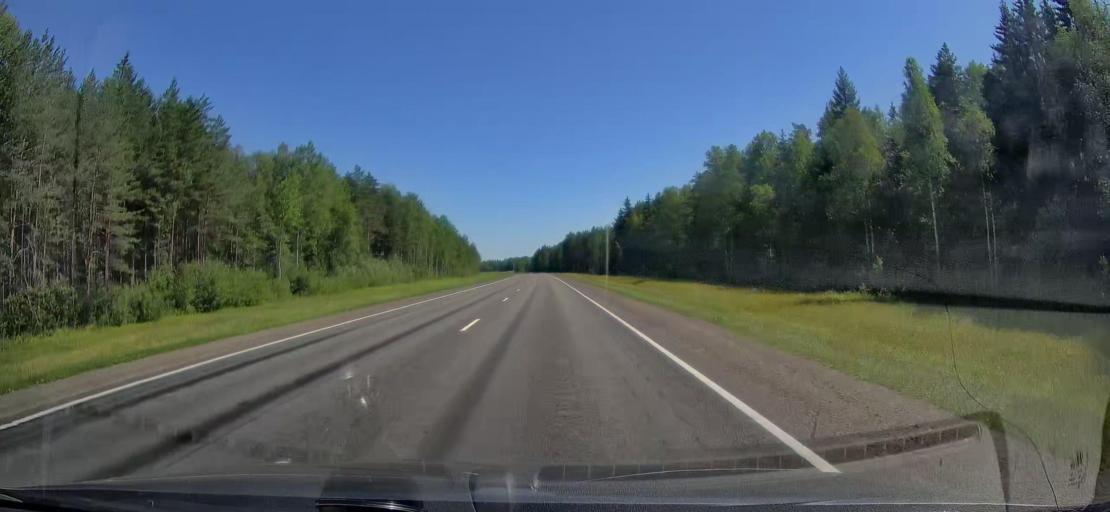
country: RU
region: Tverskaya
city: Ves'yegonsk
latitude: 58.9216
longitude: 37.2045
